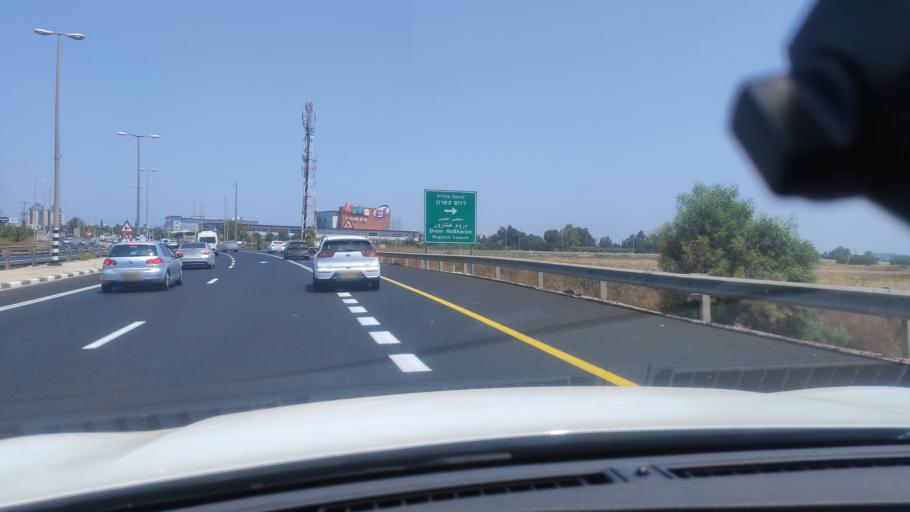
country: IL
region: Central District
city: Hod HaSharon
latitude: 32.1272
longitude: 34.9040
